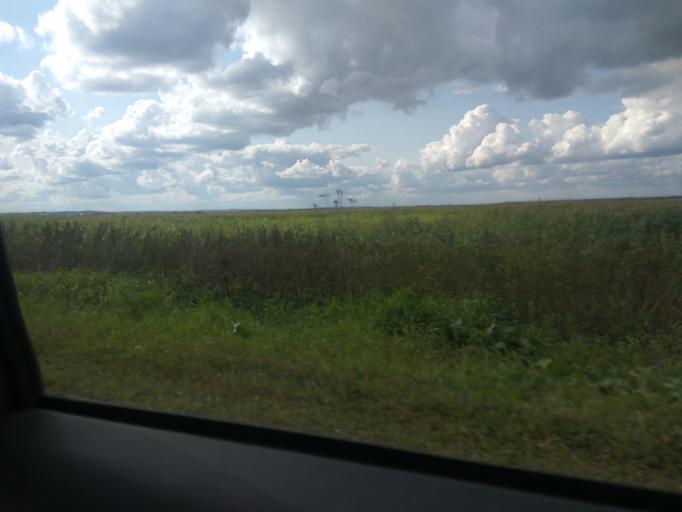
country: RU
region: Moskovskaya
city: Ramenskoye
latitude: 55.5148
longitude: 38.2659
